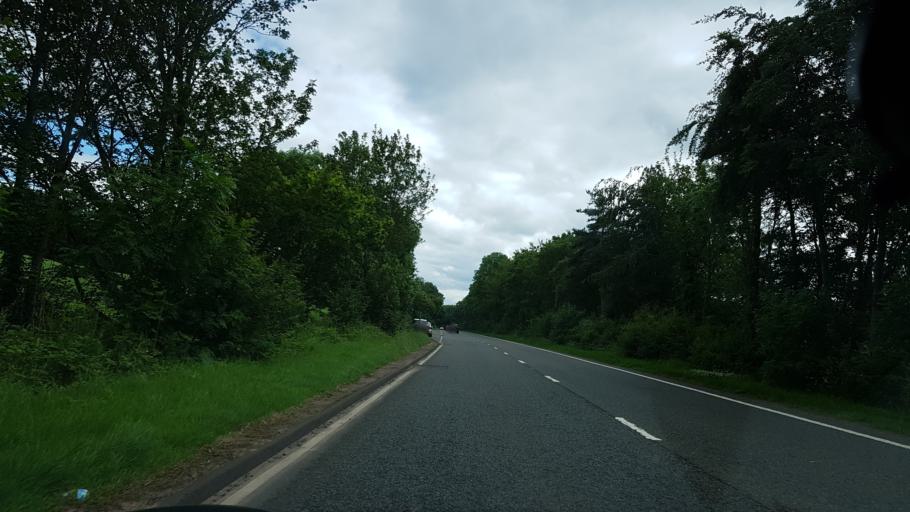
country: GB
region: Wales
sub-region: Monmouthshire
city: Abergavenny
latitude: 51.8176
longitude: -3.0082
